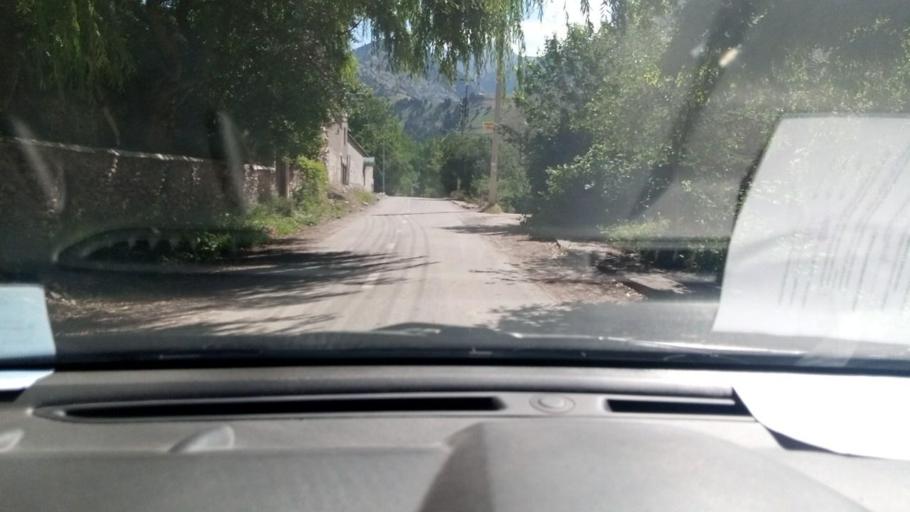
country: UZ
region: Toshkent
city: Yangiobod
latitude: 41.1216
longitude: 70.1001
